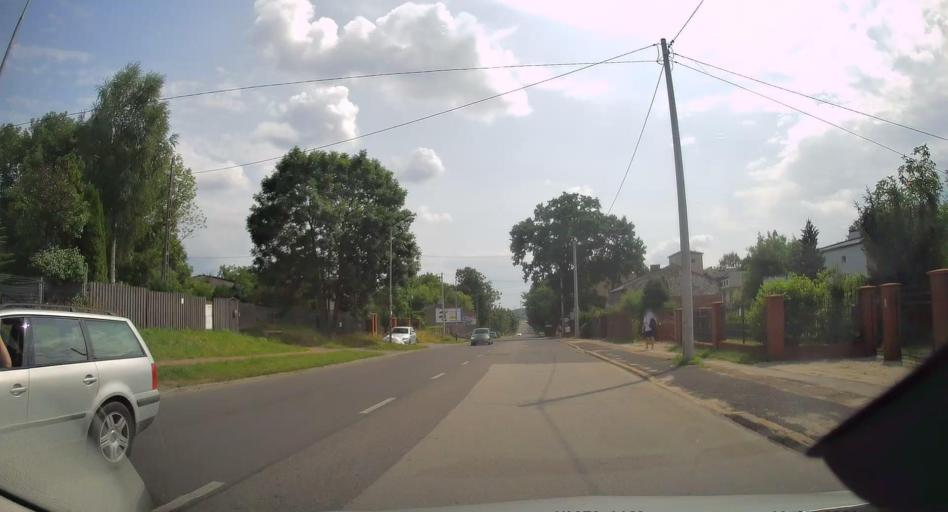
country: PL
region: Silesian Voivodeship
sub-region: Czestochowa
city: Czestochowa
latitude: 50.8104
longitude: 19.0830
